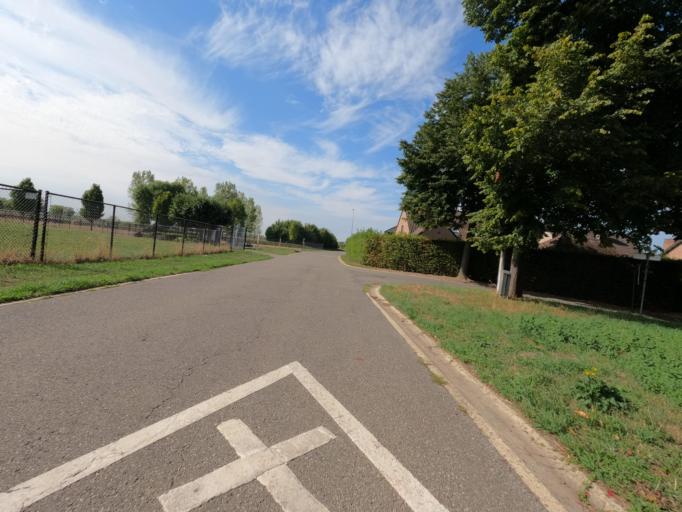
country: BE
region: Flanders
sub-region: Provincie Limburg
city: Maaseik
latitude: 51.1010
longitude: 5.8081
